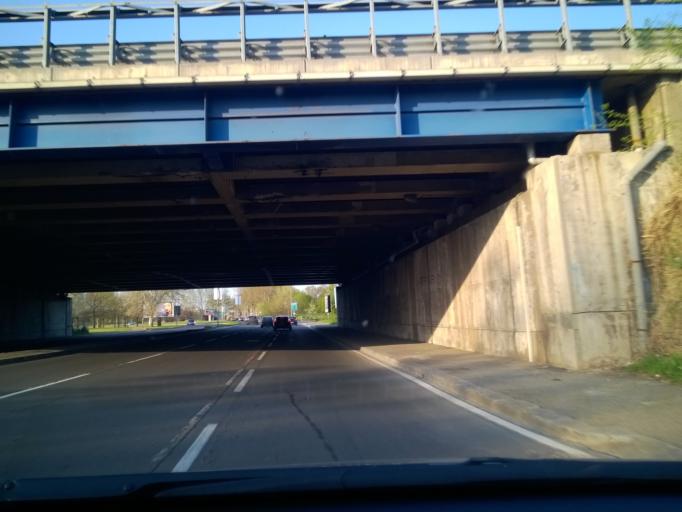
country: IT
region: Emilia-Romagna
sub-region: Provincia di Bologna
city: Bologna
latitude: 44.5229
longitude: 11.3641
